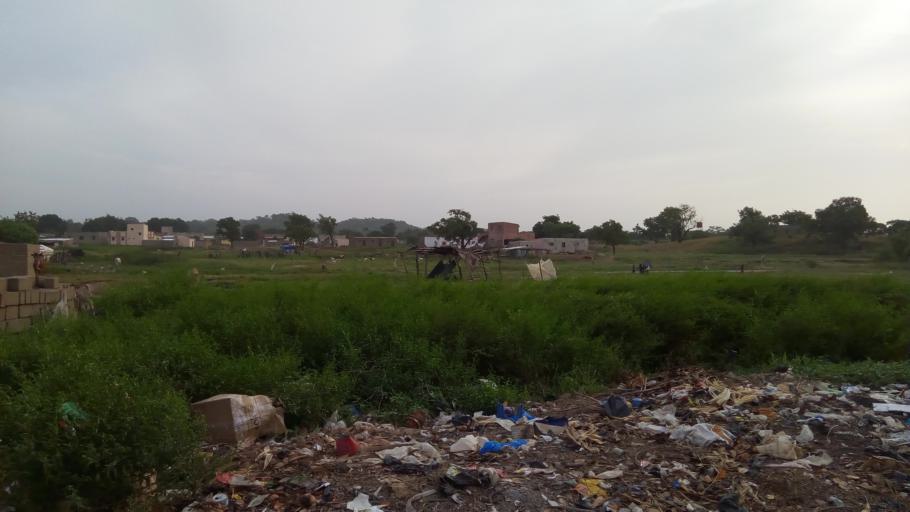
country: ML
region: Koulikoro
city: Kangaba
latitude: 11.6806
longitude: -8.6571
